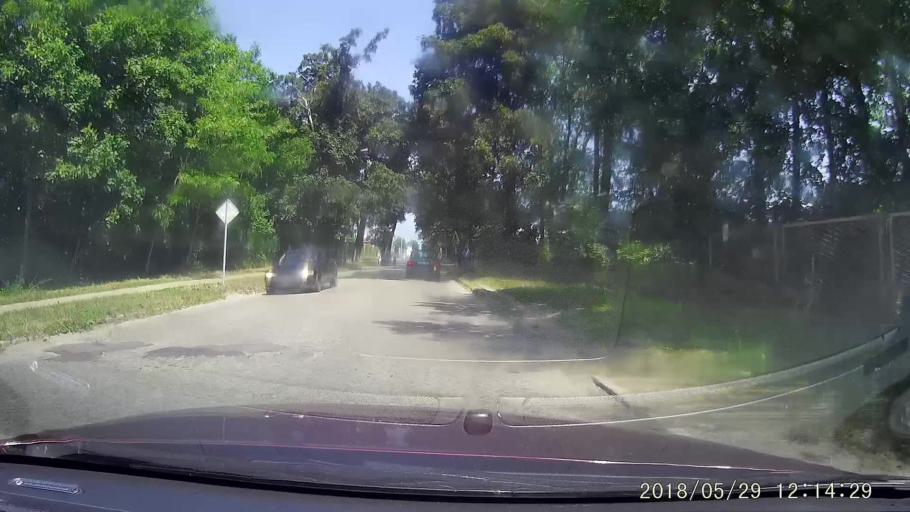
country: PL
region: Lower Silesian Voivodeship
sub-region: Powiat zgorzelecki
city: Zgorzelec
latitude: 51.1688
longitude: 15.0116
